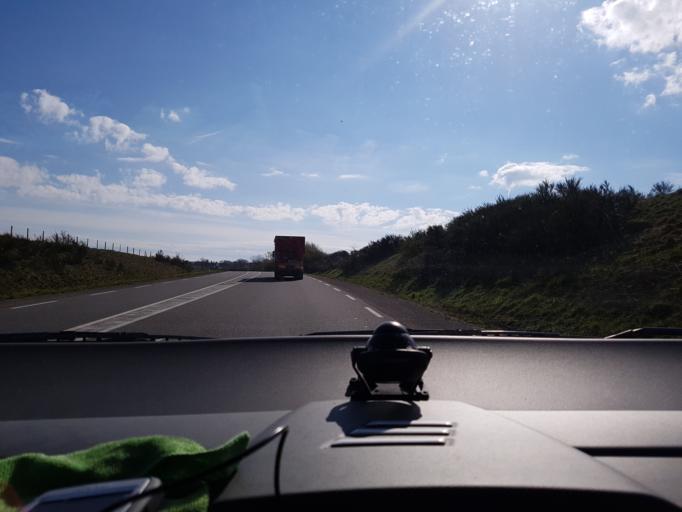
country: FR
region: Midi-Pyrenees
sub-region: Departement de l'Aveyron
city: Colombies
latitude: 44.3967
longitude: 2.3137
